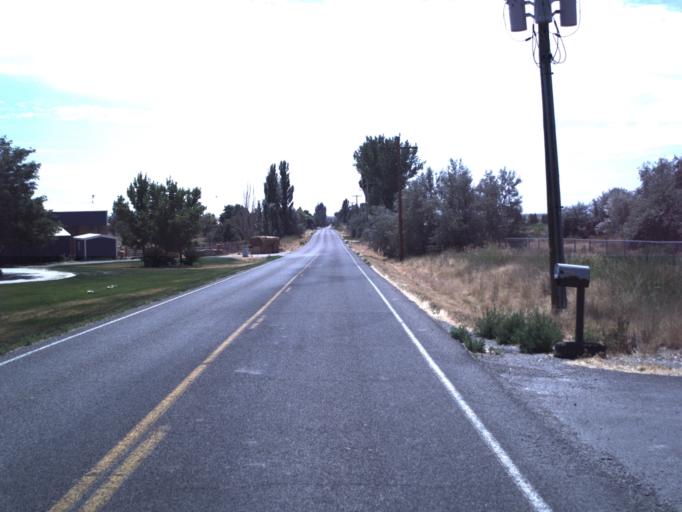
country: US
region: Utah
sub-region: Box Elder County
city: Tremonton
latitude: 41.6596
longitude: -112.2962
